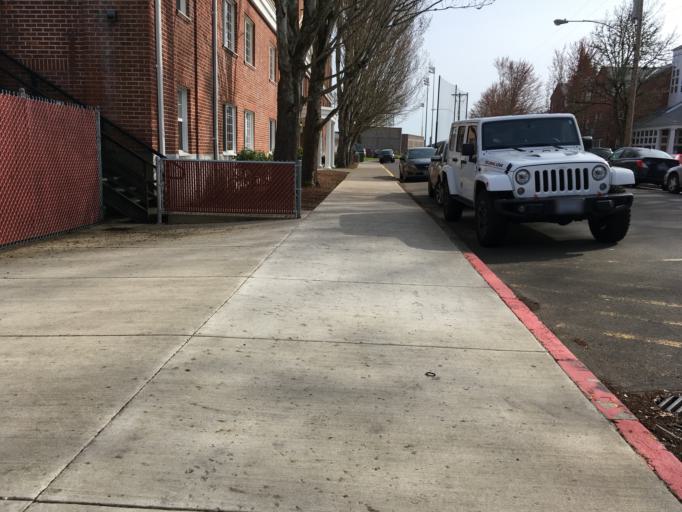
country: US
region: Oregon
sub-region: Yamhill County
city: McMinnville
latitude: 45.1992
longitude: -123.1980
